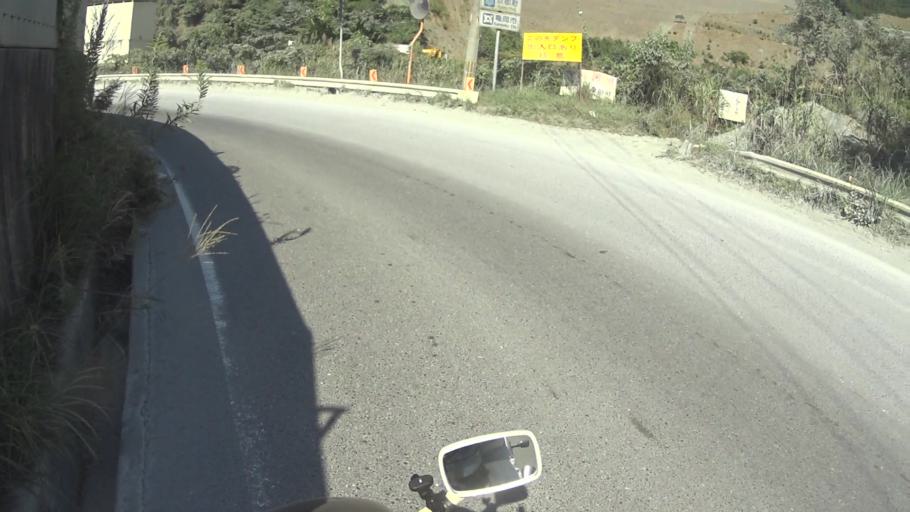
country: JP
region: Osaka
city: Takatsuki
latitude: 34.9167
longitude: 135.5712
